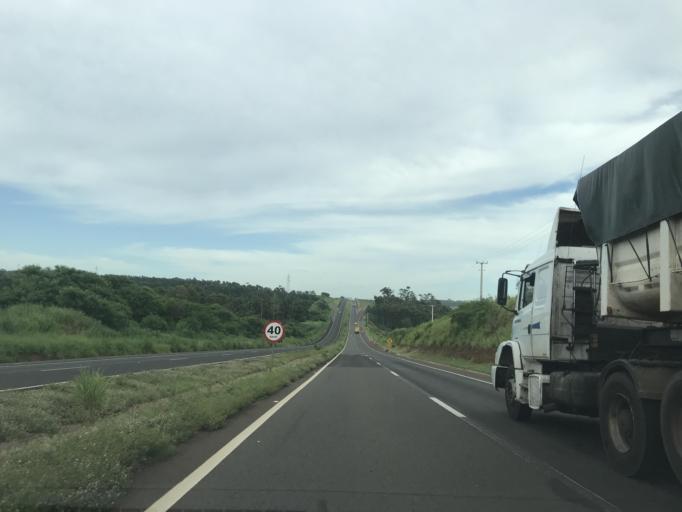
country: BR
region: Parana
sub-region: Alto Parana
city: Alto Parana
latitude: -23.1149
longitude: -52.3274
